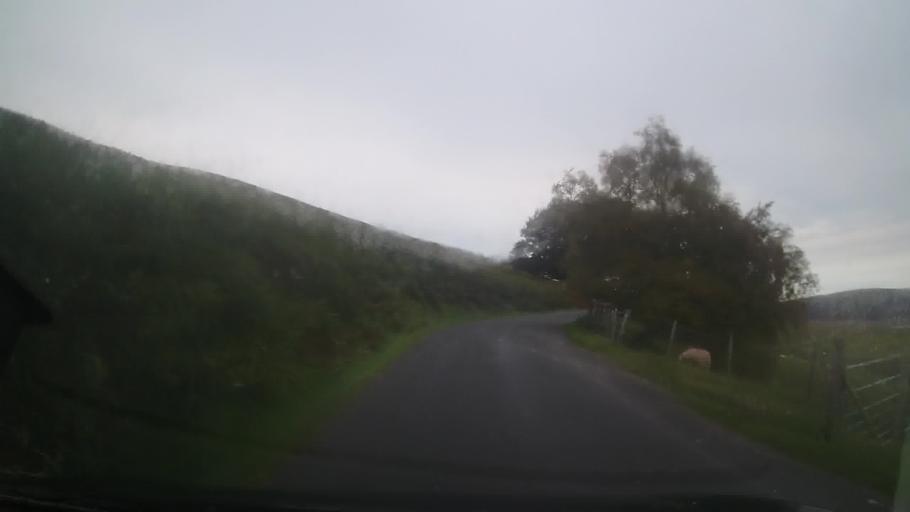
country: GB
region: Wales
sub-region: Sir Powys
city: Rhayader
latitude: 52.3139
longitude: -3.6325
